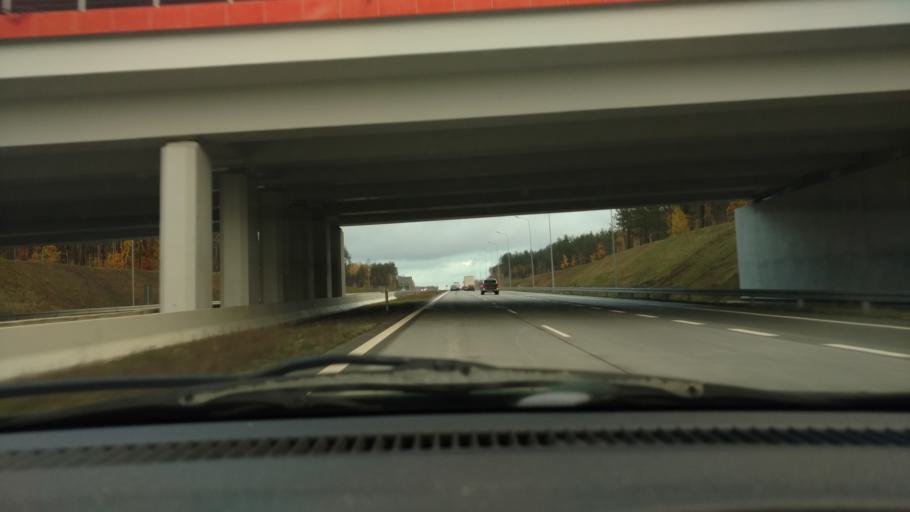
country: PL
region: Lodz Voivodeship
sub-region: Powiat lodzki wschodni
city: Tuszyn
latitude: 51.6508
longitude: 19.5774
